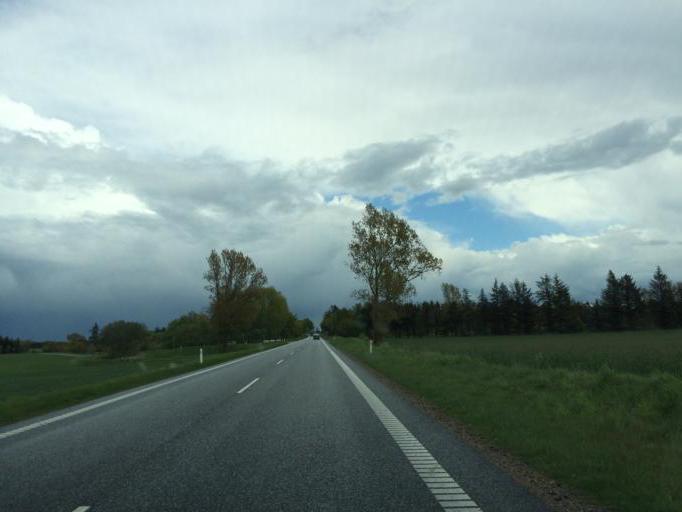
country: DK
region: North Denmark
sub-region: Vesthimmerland Kommune
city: Farso
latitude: 56.6059
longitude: 9.3217
